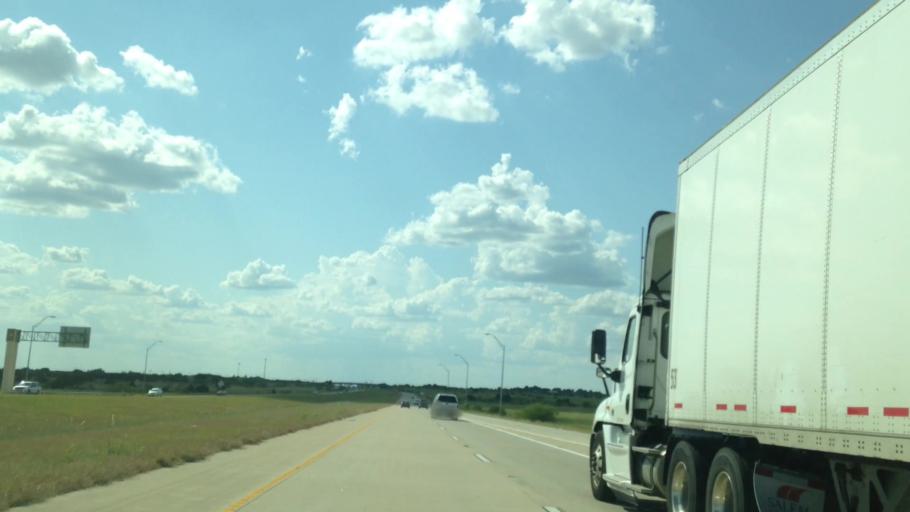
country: US
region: Texas
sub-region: Travis County
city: Onion Creek
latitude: 30.0854
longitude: -97.7384
